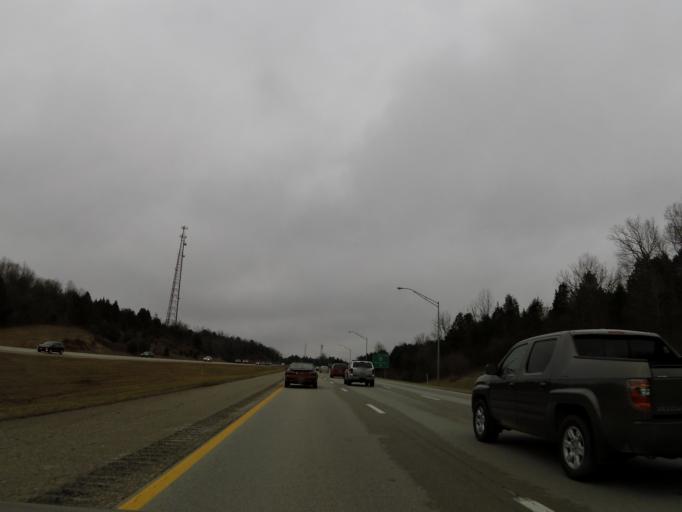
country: US
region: Kentucky
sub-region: Scott County
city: Georgetown
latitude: 38.3855
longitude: -84.5744
